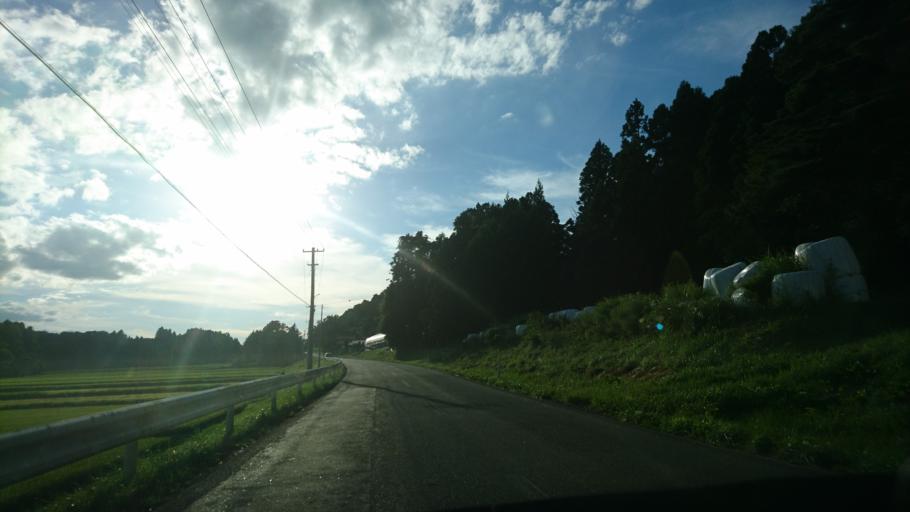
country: JP
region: Iwate
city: Ichinoseki
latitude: 38.8340
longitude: 141.1172
